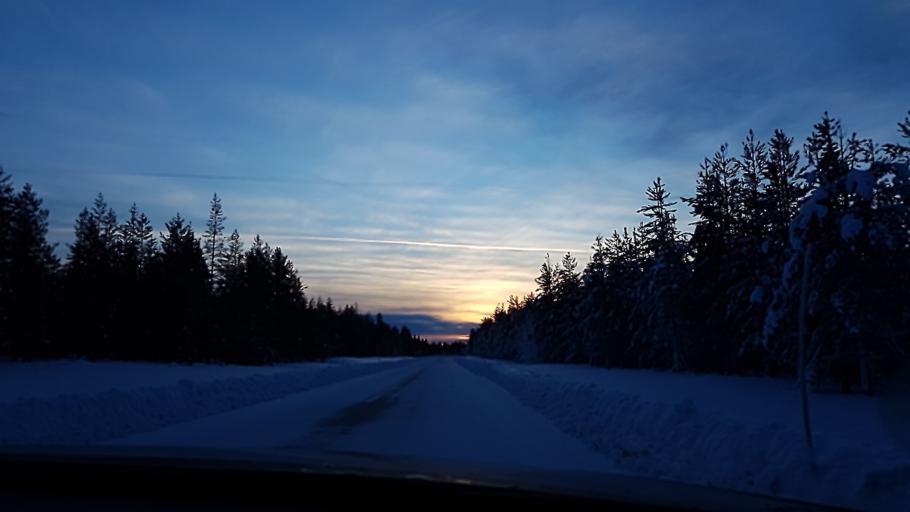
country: SE
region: Norrbotten
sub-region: Jokkmokks Kommun
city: Jokkmokk
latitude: 66.0750
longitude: 20.0737
